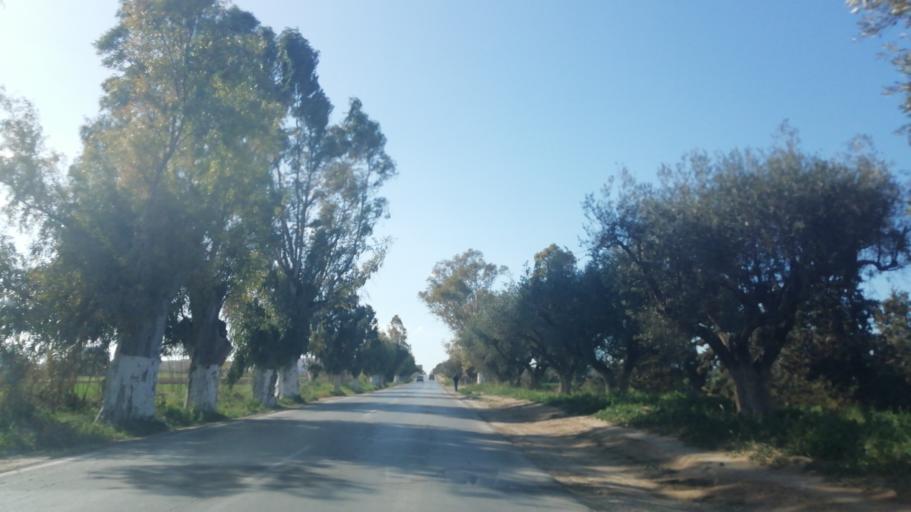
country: DZ
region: Mostaganem
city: Mostaganem
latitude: 35.9988
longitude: 0.3171
